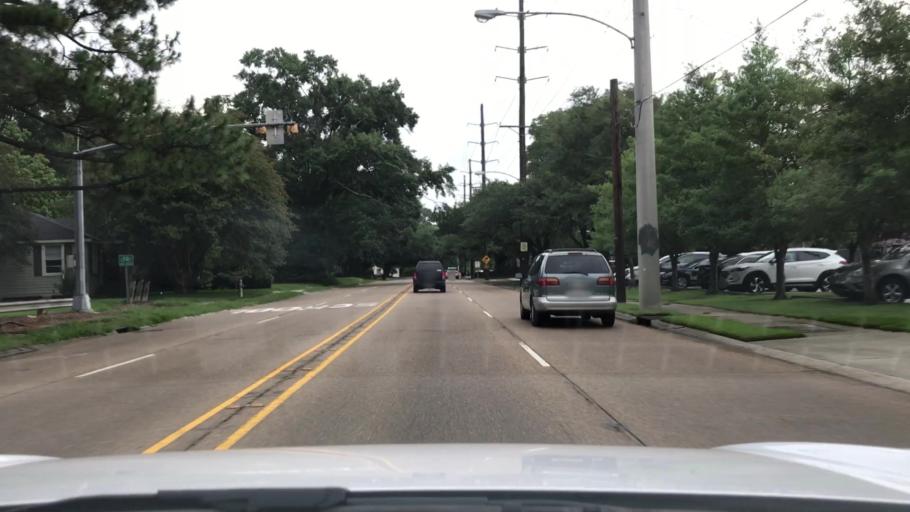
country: US
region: Louisiana
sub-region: East Baton Rouge Parish
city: Baton Rouge
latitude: 30.4325
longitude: -91.1349
